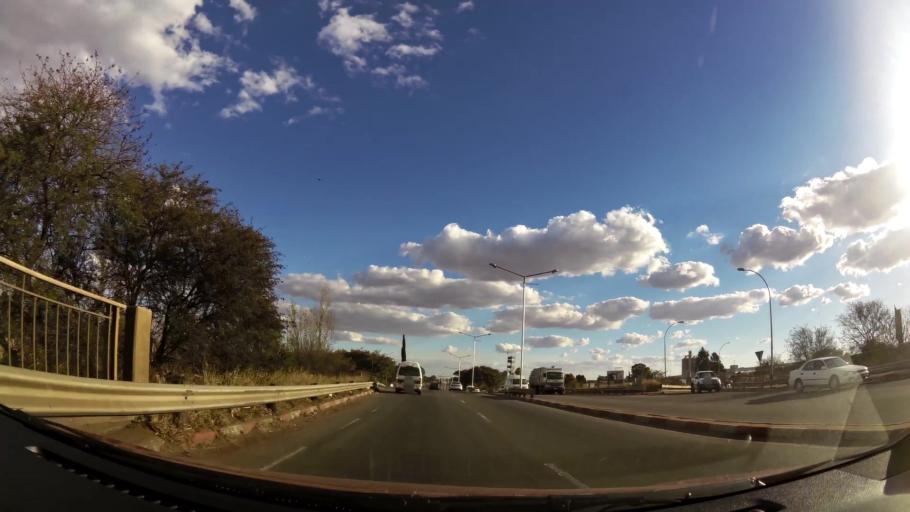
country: ZA
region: North-West
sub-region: Dr Kenneth Kaunda District Municipality
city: Potchefstroom
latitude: -26.7156
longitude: 27.0862
